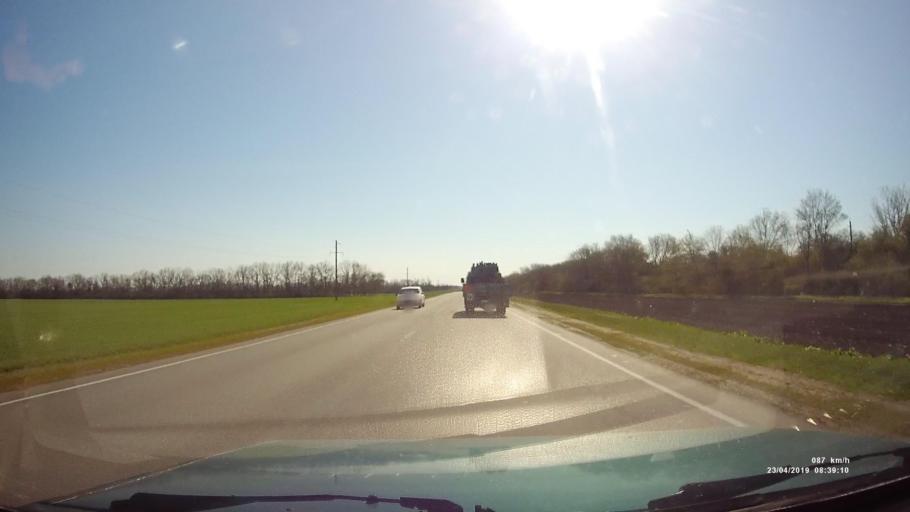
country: RU
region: Rostov
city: Gigant
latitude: 46.5271
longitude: 41.2016
